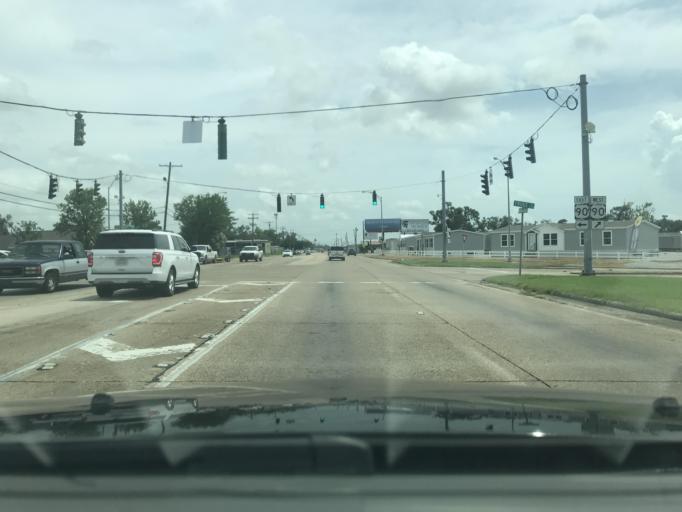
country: US
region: Louisiana
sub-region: Calcasieu Parish
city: Lake Charles
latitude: 30.2352
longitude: -93.1804
